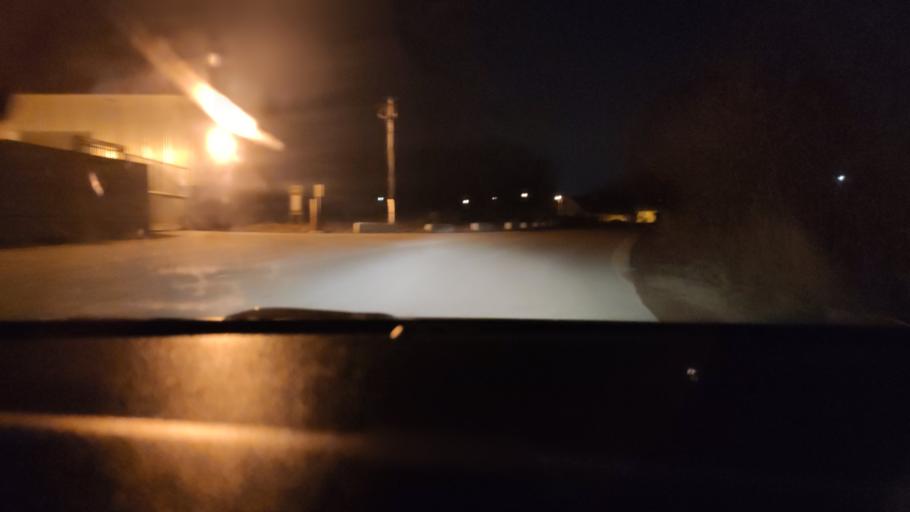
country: RU
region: Tatarstan
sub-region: Gorod Kazan'
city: Kazan
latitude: 55.8478
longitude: 49.1955
